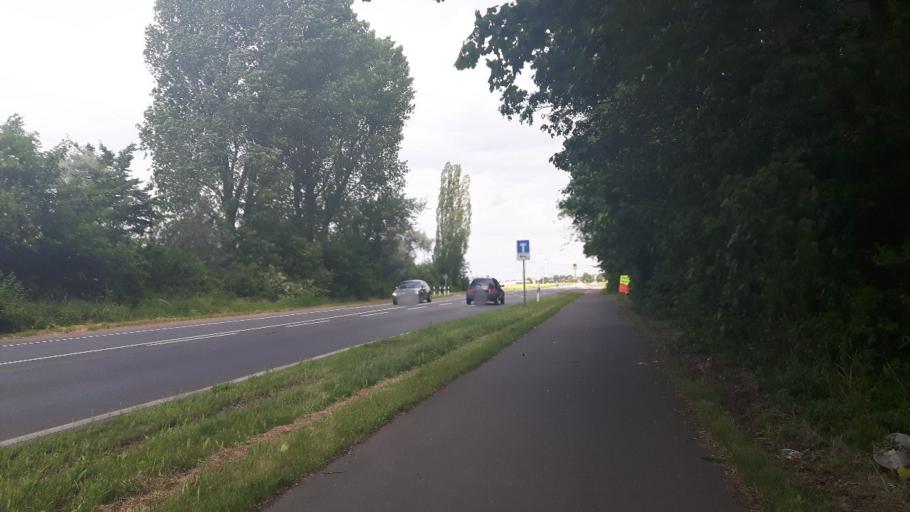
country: DE
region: Berlin
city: Wartenberg
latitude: 52.5957
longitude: 13.5033
